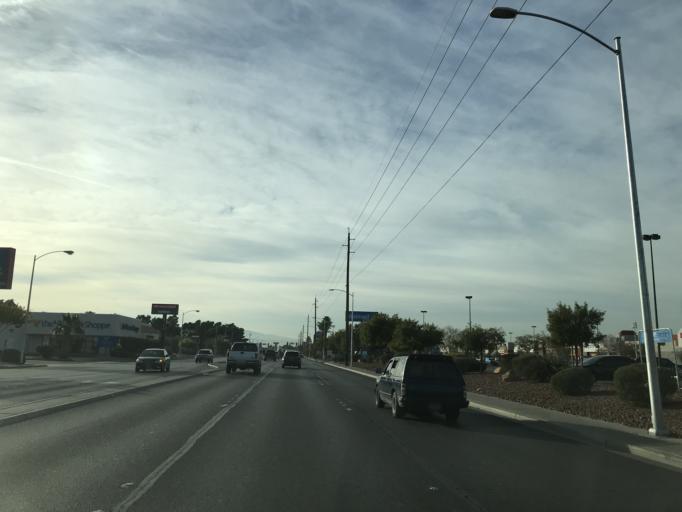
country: US
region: Nevada
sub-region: Clark County
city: Sunrise Manor
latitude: 36.1645
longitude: -115.0623
